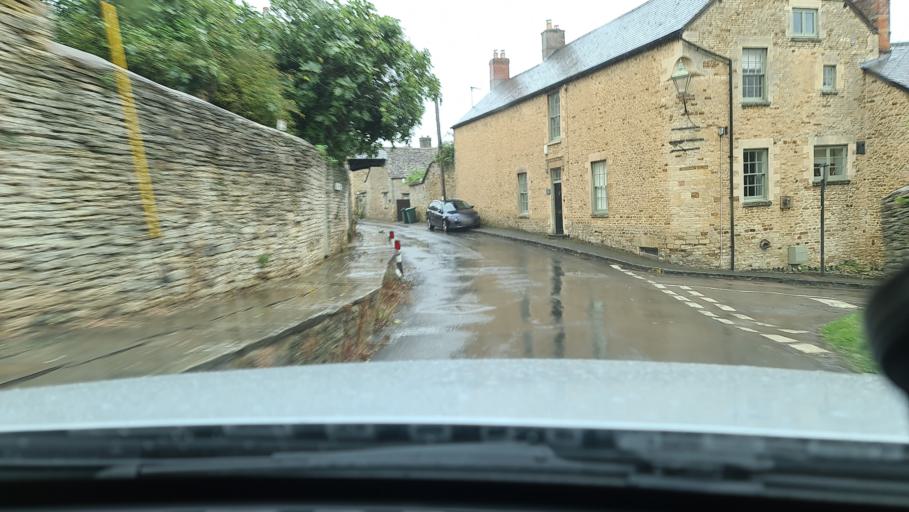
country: GB
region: England
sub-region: Oxfordshire
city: Somerton
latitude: 51.9311
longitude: -1.3142
